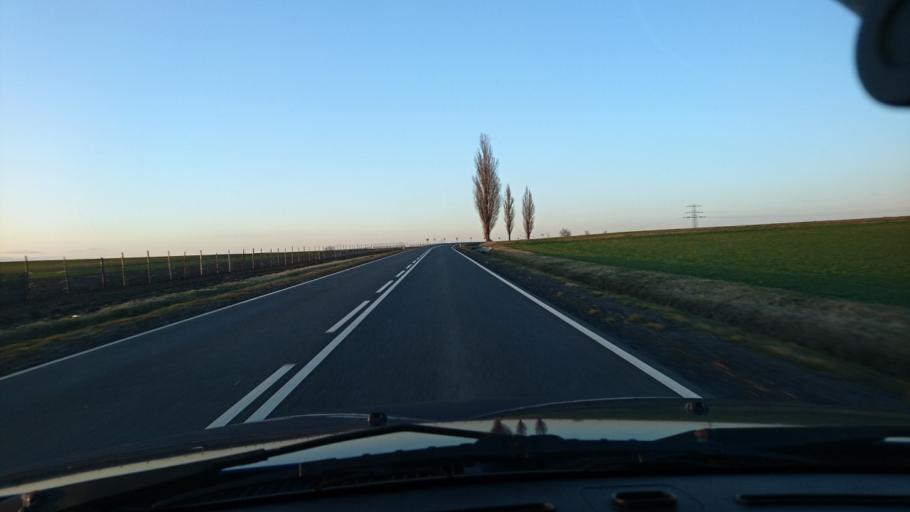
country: PL
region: Silesian Voivodeship
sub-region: Powiat gliwicki
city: Wielowies
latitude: 50.4836
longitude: 18.6054
